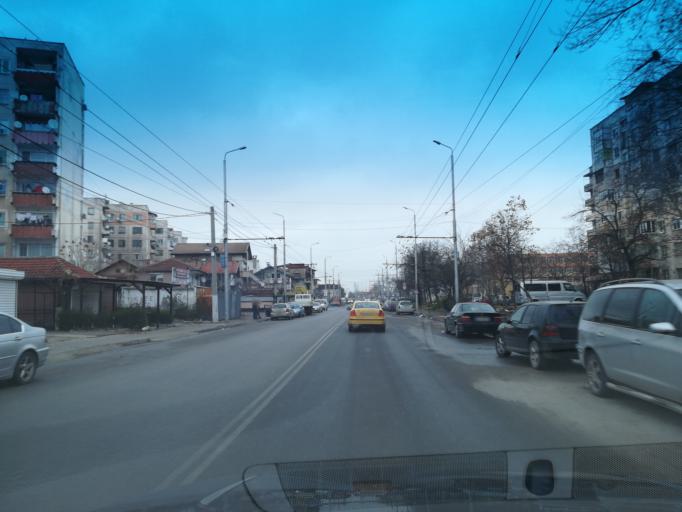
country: BG
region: Plovdiv
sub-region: Obshtina Plovdiv
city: Plovdiv
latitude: 42.1554
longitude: 24.7876
